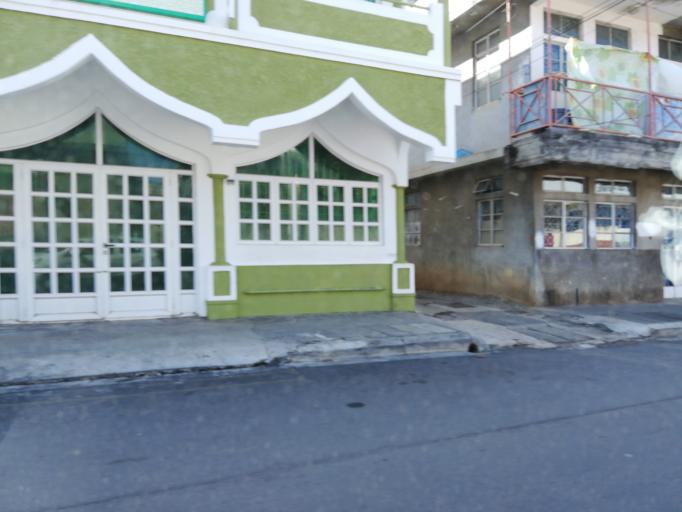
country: MU
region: Port Louis
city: Port Louis
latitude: -20.1636
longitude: 57.4845
